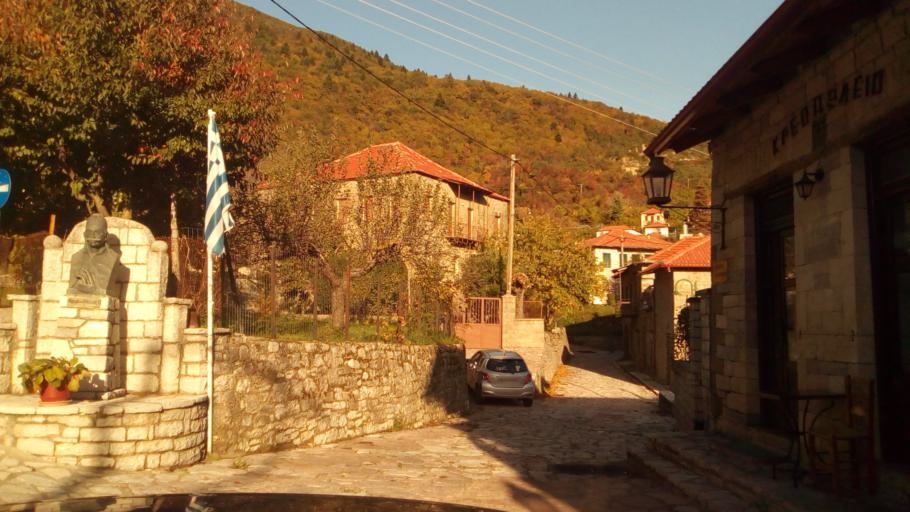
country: GR
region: West Greece
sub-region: Nomos Aitolias kai Akarnanias
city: Thermo
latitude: 38.6002
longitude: 21.7919
